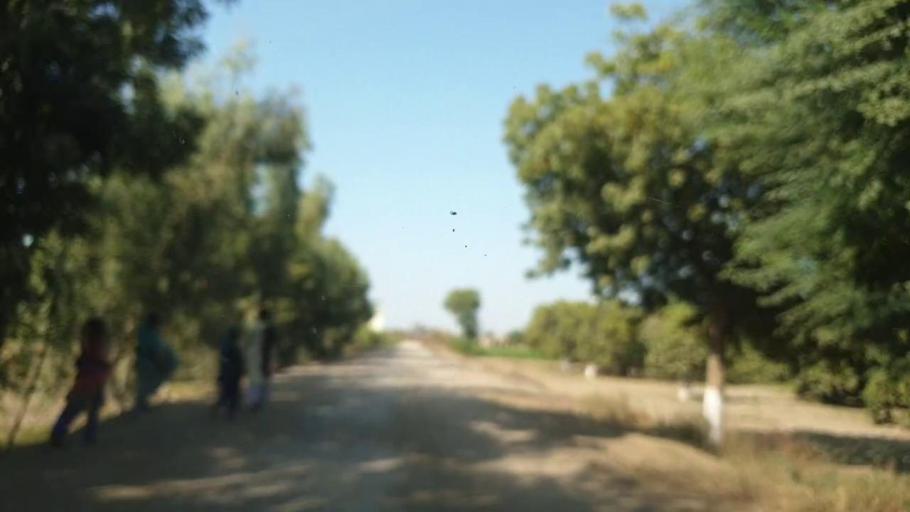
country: PK
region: Sindh
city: Nabisar
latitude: 25.0374
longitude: 69.4867
